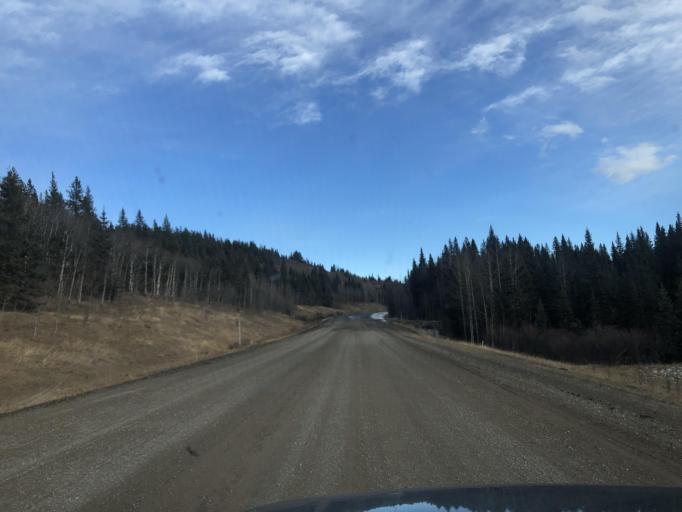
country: CA
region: Alberta
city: Cochrane
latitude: 51.0434
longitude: -114.7571
